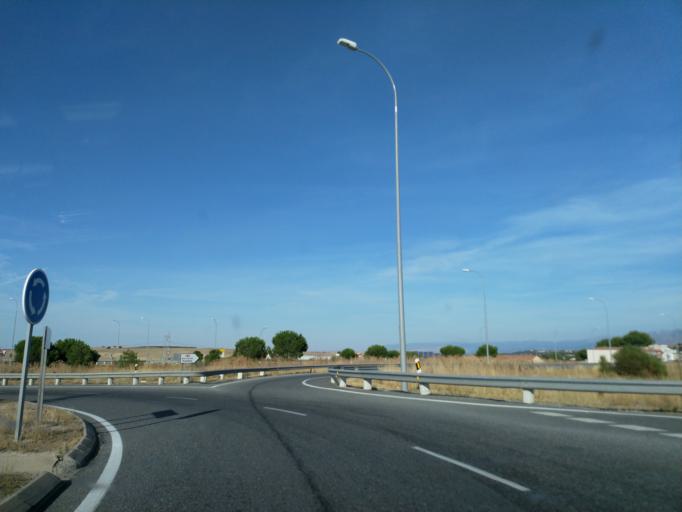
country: ES
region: Castille and Leon
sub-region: Provincia de Segovia
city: Villacastin
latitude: 40.7825
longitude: -4.4210
